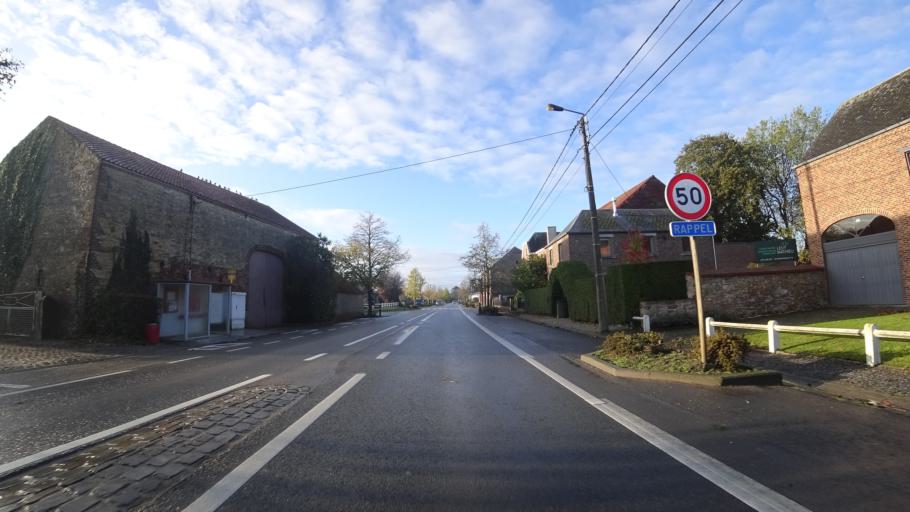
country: BE
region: Wallonia
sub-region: Province de Namur
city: Gembloux
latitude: 50.5347
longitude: 4.7812
